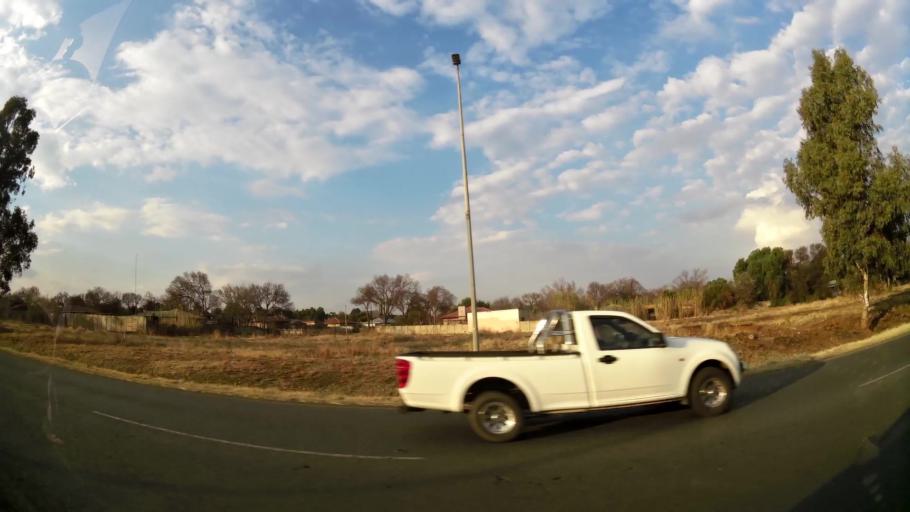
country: ZA
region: Gauteng
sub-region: Sedibeng District Municipality
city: Vanderbijlpark
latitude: -26.7020
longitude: 27.8110
